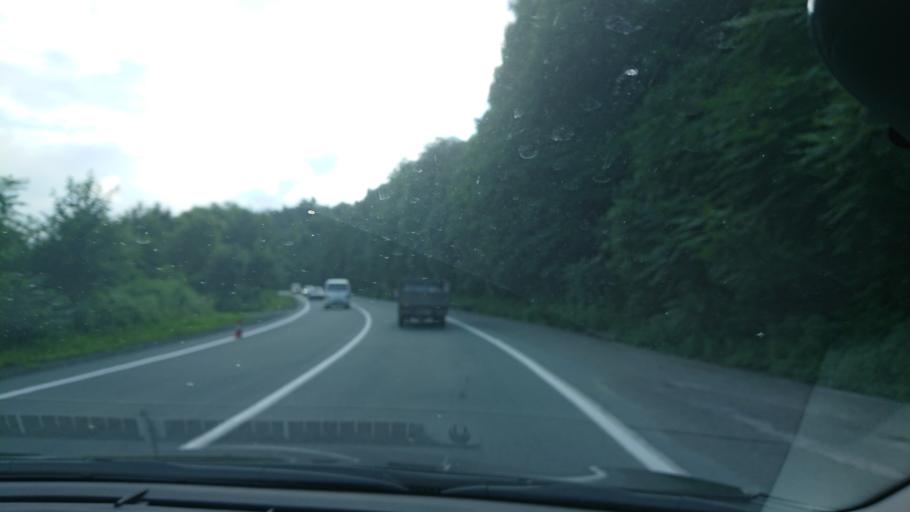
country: TR
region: Rize
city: Rize
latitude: 41.0124
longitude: 40.5582
